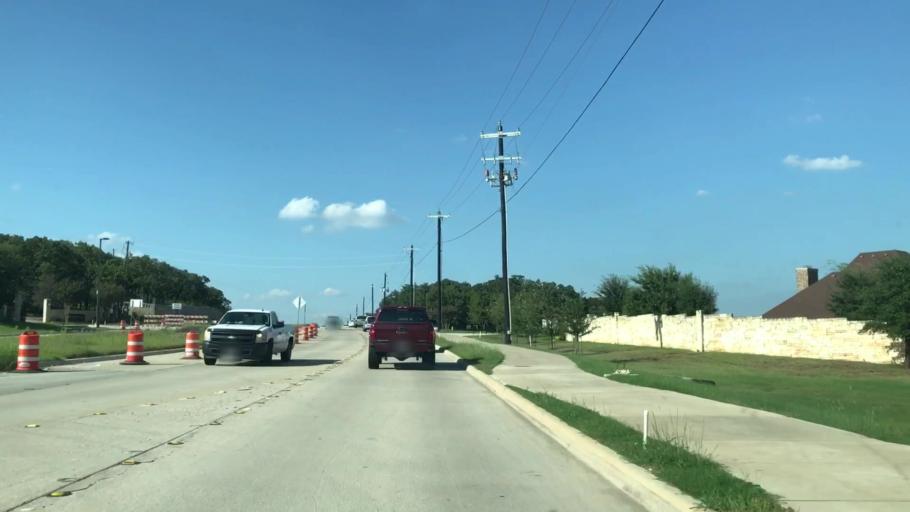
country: US
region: Texas
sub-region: Denton County
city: Trophy Club
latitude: 32.9520
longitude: -97.1856
